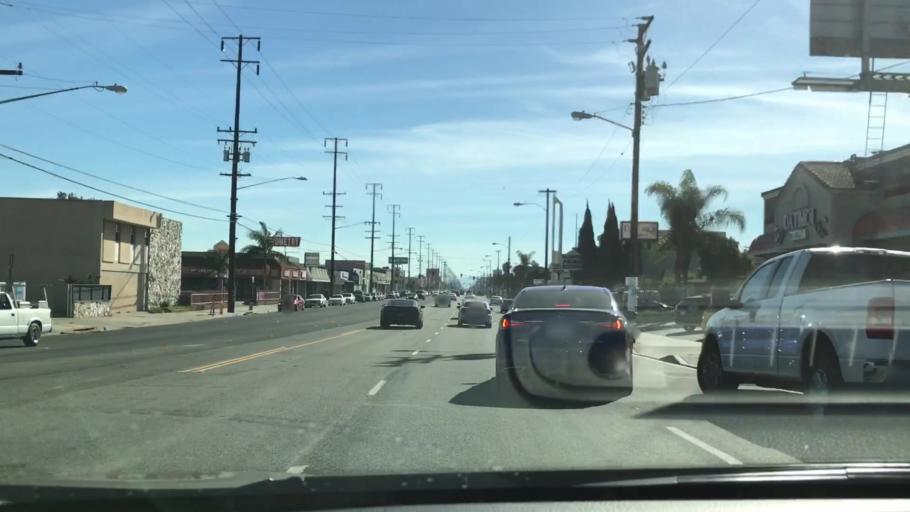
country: US
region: California
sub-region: Los Angeles County
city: Alondra Park
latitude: 33.9009
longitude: -118.3266
